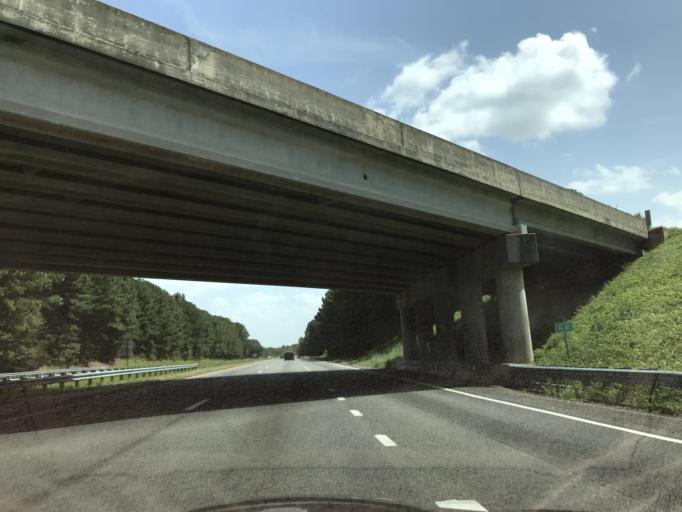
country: US
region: North Carolina
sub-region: Sampson County
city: Plain View
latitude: 35.2260
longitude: -78.3487
